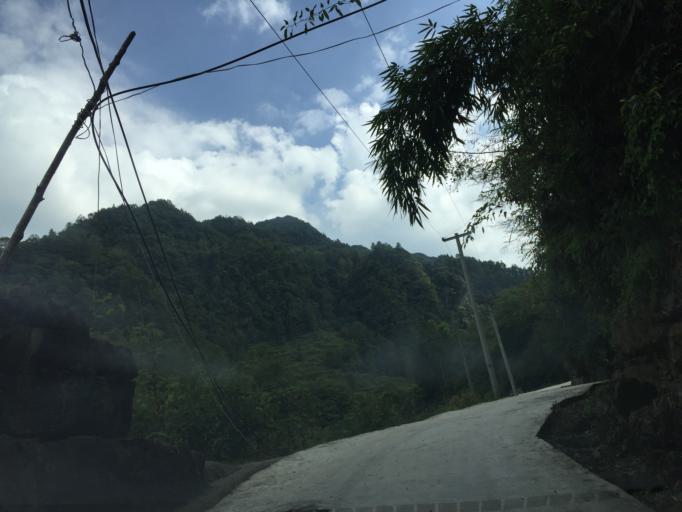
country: CN
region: Guizhou Sheng
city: Quankou
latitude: 28.5395
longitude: 108.1227
